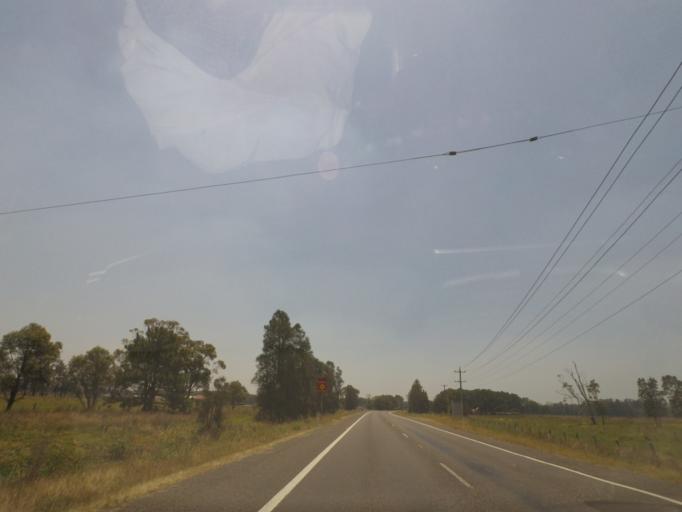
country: AU
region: New South Wales
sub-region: Port Stephens Shire
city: Medowie
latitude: -32.7957
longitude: 151.8933
